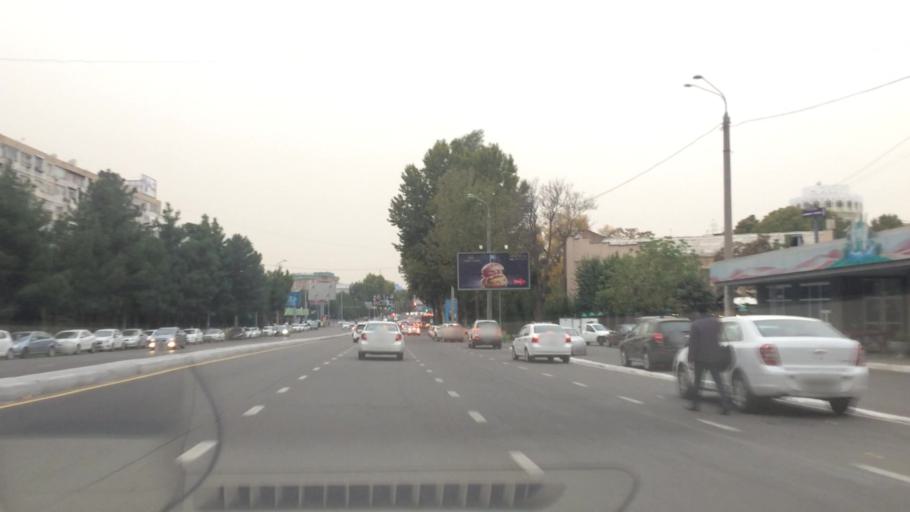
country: UZ
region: Toshkent Shahri
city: Tashkent
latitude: 41.3048
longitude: 69.2817
